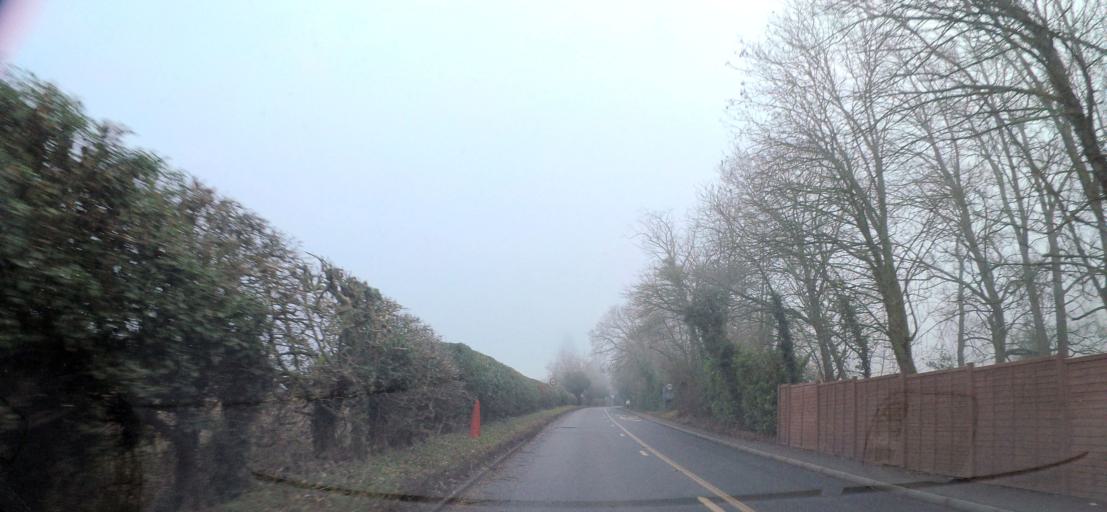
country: GB
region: England
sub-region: West Berkshire
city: Calcot
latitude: 51.4092
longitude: -1.0439
